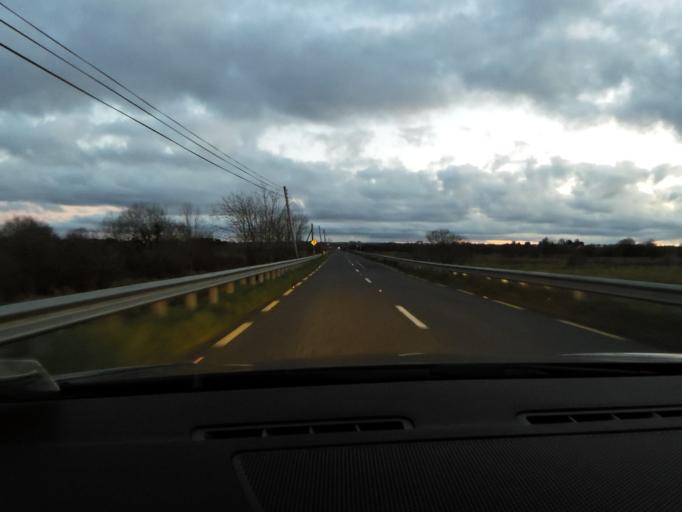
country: IE
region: Connaught
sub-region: Roscommon
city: Roscommon
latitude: 53.7905
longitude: -8.2424
